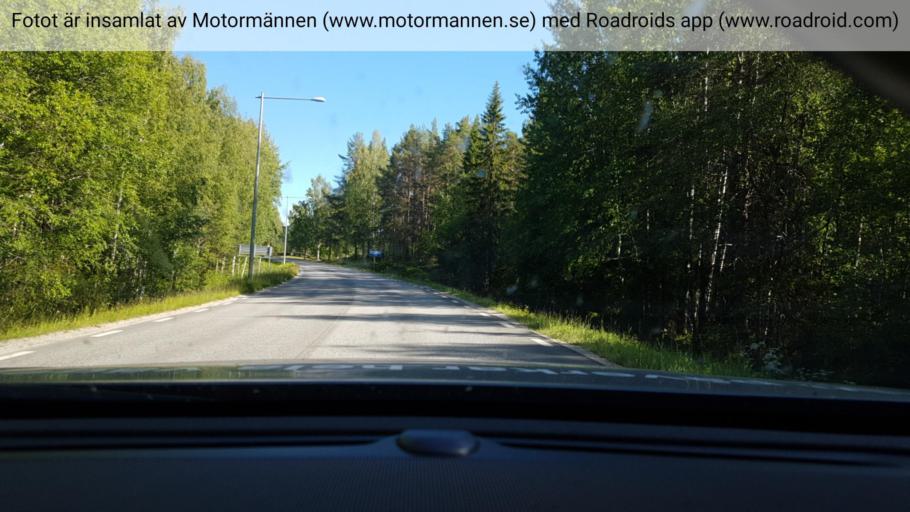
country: SE
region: Vaesterbotten
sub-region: Lycksele Kommun
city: Lycksele
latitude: 64.6095
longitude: 18.6468
